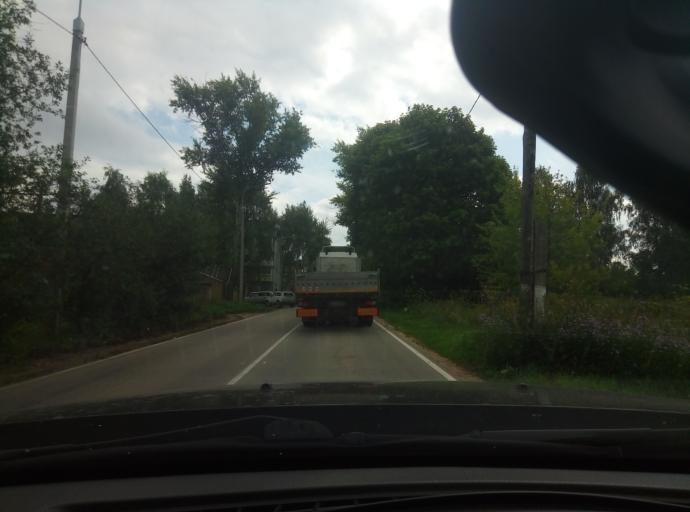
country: RU
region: Tula
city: Borodinskiy
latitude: 53.9961
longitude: 37.8088
